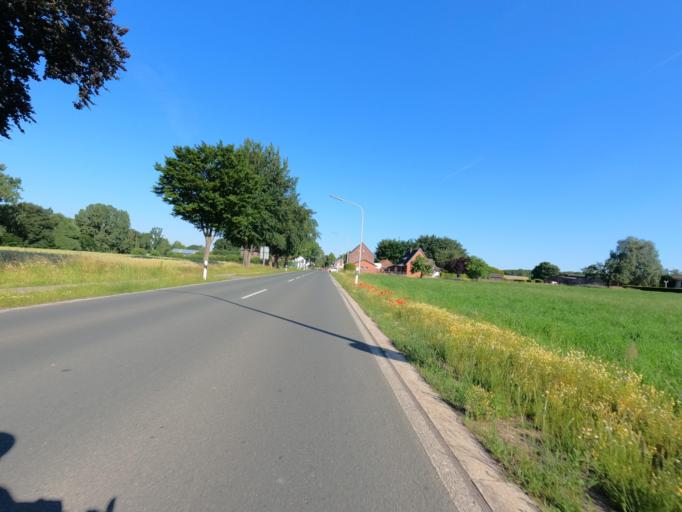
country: NL
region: Limburg
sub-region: Gemeente Roerdalen
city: Vlodrop
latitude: 51.1125
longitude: 6.0594
